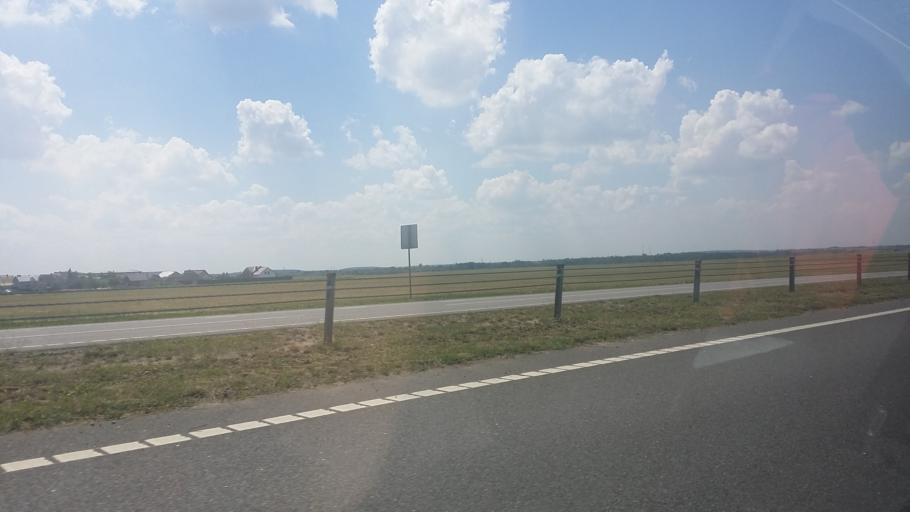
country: BY
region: Minsk
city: Luhavaya Slabada
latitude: 53.7616
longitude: 27.9103
